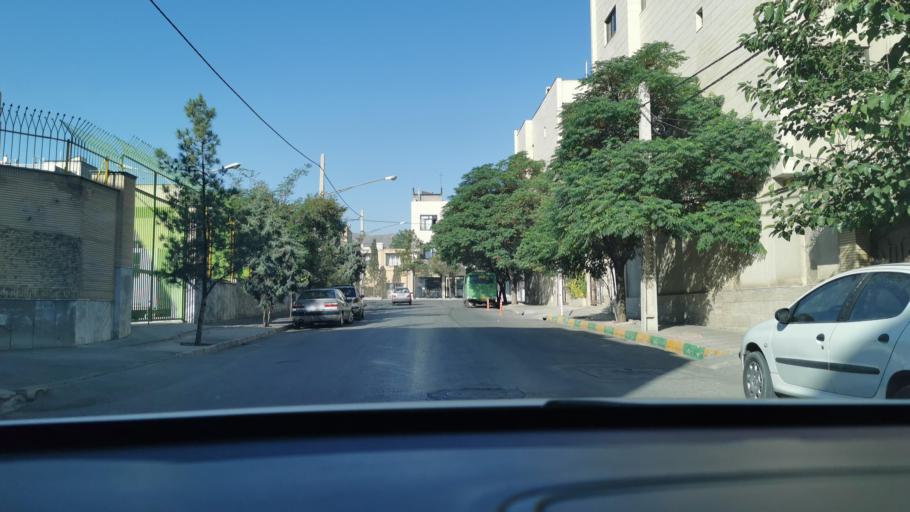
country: IR
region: Razavi Khorasan
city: Mashhad
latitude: 36.3095
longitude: 59.5101
